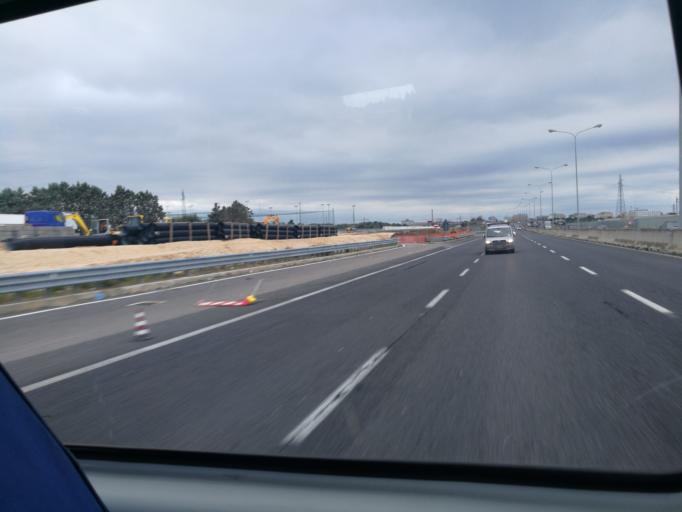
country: IT
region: Apulia
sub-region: Provincia di Bari
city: Triggiano
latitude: 41.0986
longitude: 16.9063
